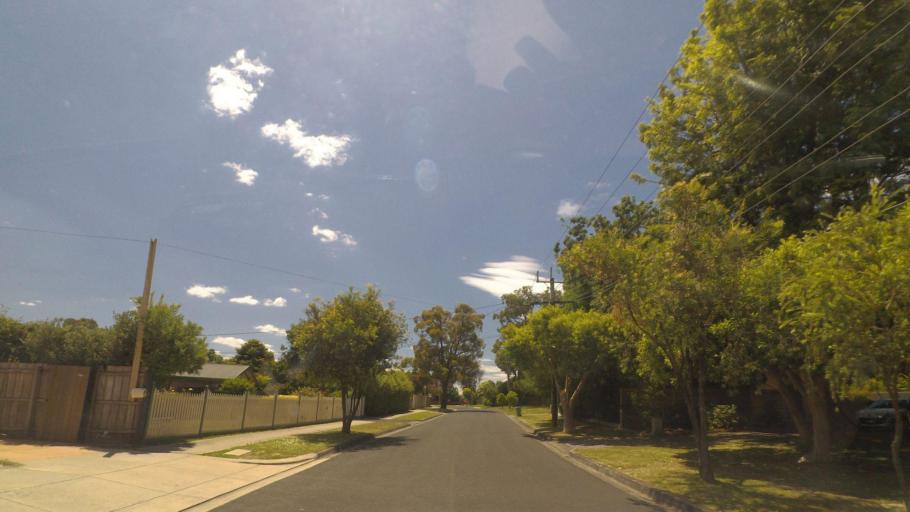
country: AU
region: Victoria
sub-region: Yarra Ranges
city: Kilsyth
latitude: -37.8099
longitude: 145.3245
